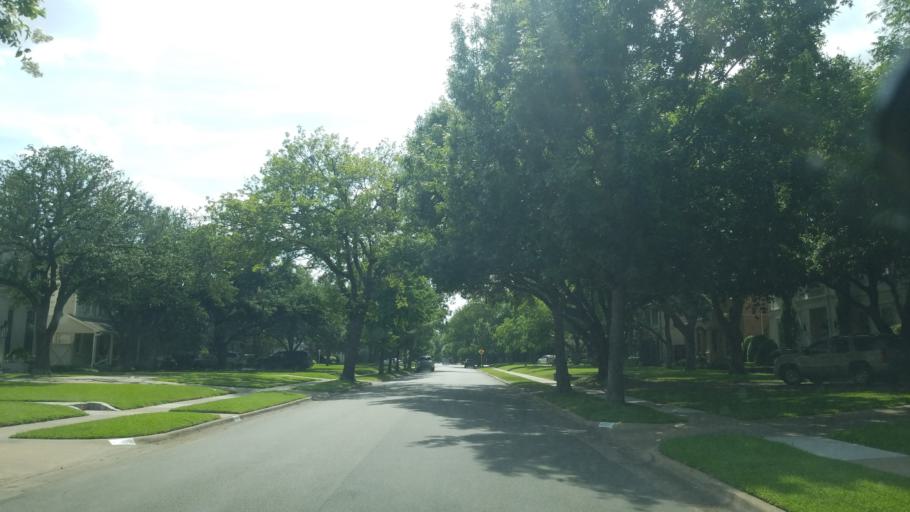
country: US
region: Texas
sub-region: Dallas County
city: University Park
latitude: 32.8570
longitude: -96.8023
